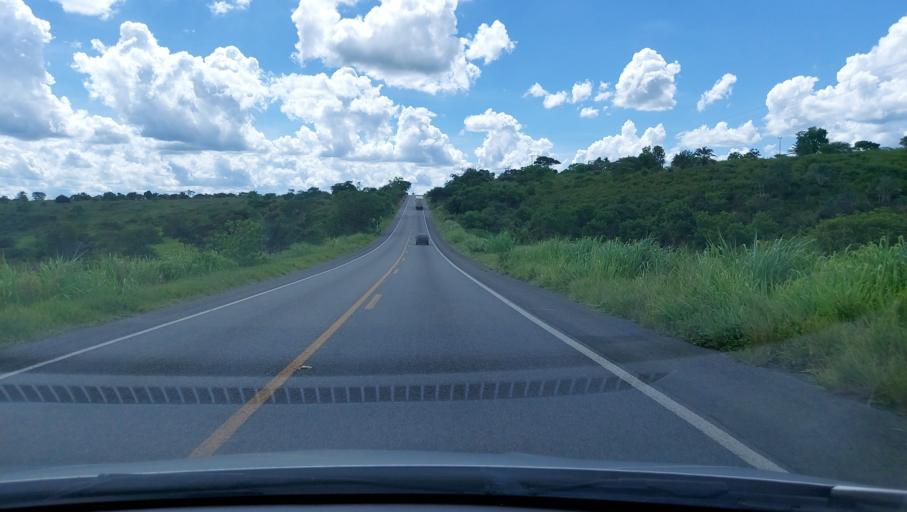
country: BR
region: Bahia
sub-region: Ruy Barbosa
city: Terra Nova
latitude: -12.4497
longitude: -40.6456
